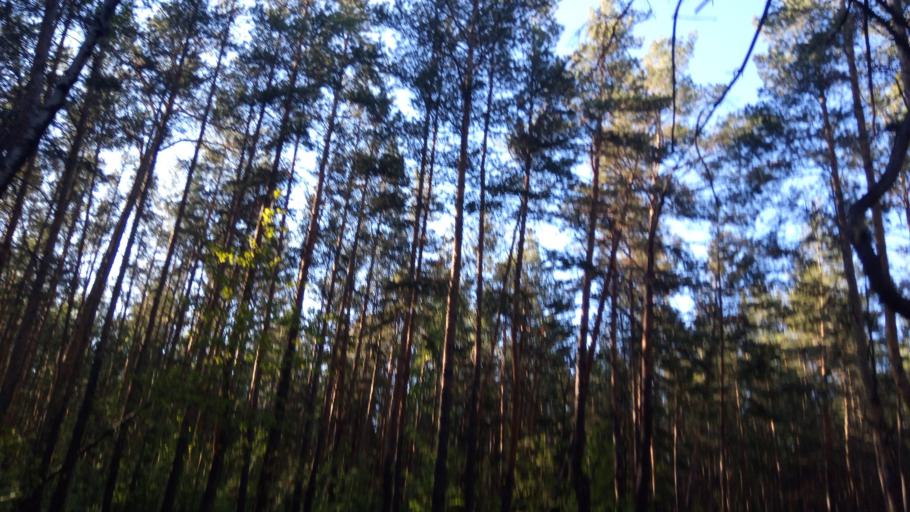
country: RU
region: Chelyabinsk
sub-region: Gorod Chelyabinsk
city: Chelyabinsk
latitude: 55.1283
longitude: 61.3397
